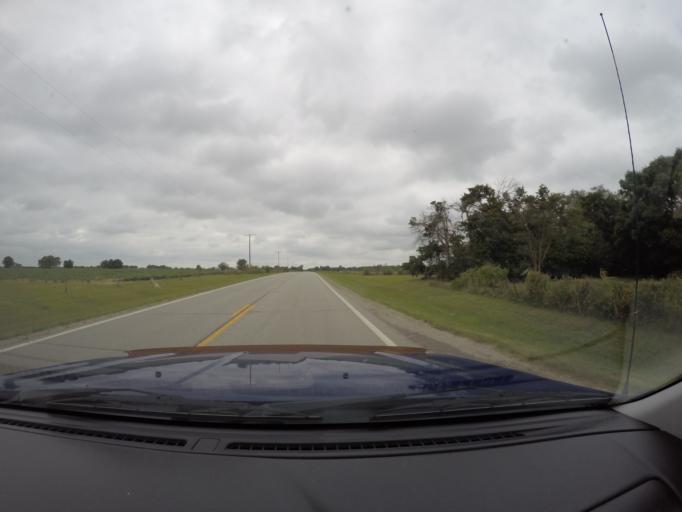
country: US
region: Kansas
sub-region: Morris County
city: Council Grove
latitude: 38.8412
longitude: -96.5785
